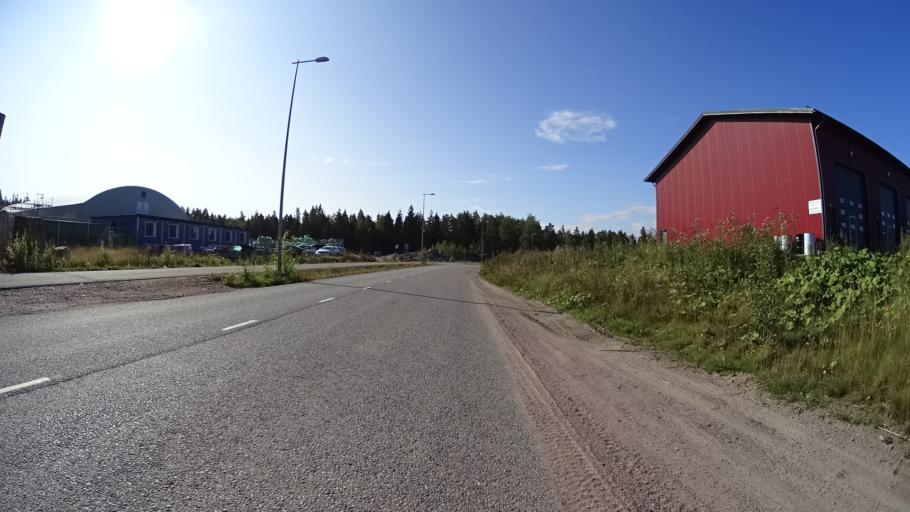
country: FI
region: Uusimaa
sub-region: Helsinki
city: Kilo
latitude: 60.2900
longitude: 24.7661
